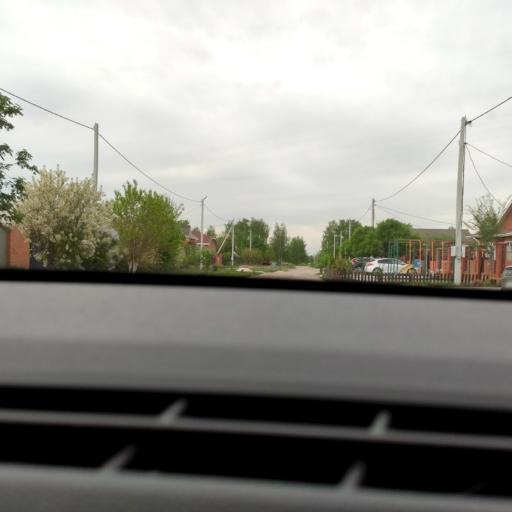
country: RU
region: Samara
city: Tol'yatti
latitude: 53.5565
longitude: 49.4090
